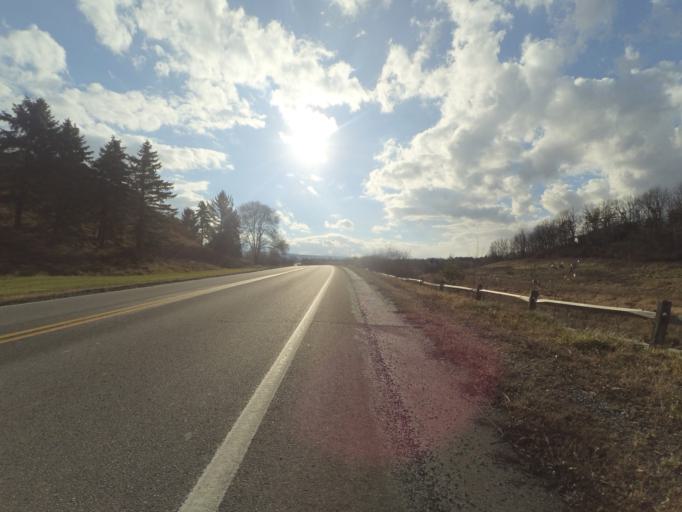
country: US
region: Pennsylvania
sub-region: Centre County
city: Lemont
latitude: 40.7890
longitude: -77.8331
